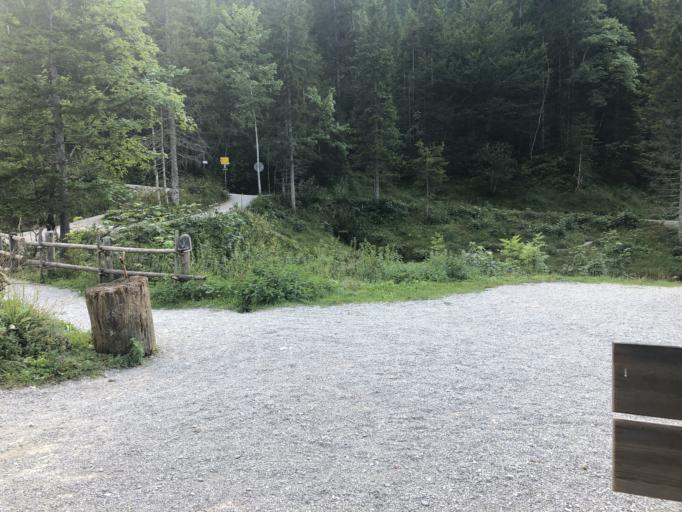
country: DE
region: Bavaria
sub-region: Upper Bavaria
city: Kreuth
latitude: 47.6108
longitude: 11.7440
